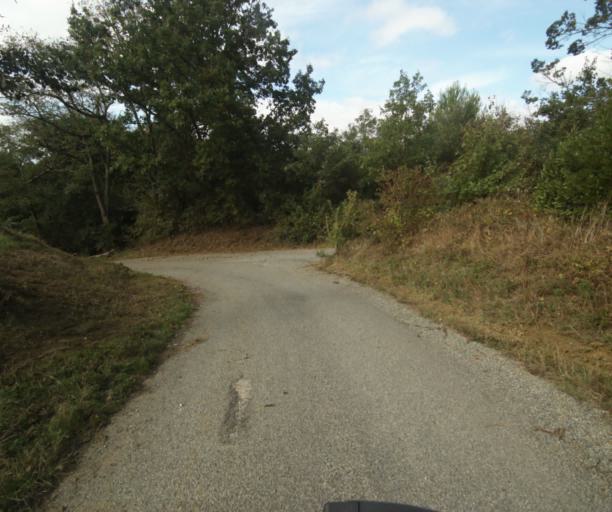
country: FR
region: Midi-Pyrenees
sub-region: Departement du Tarn-et-Garonne
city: Saint-Porquier
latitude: 43.9631
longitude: 1.1624
